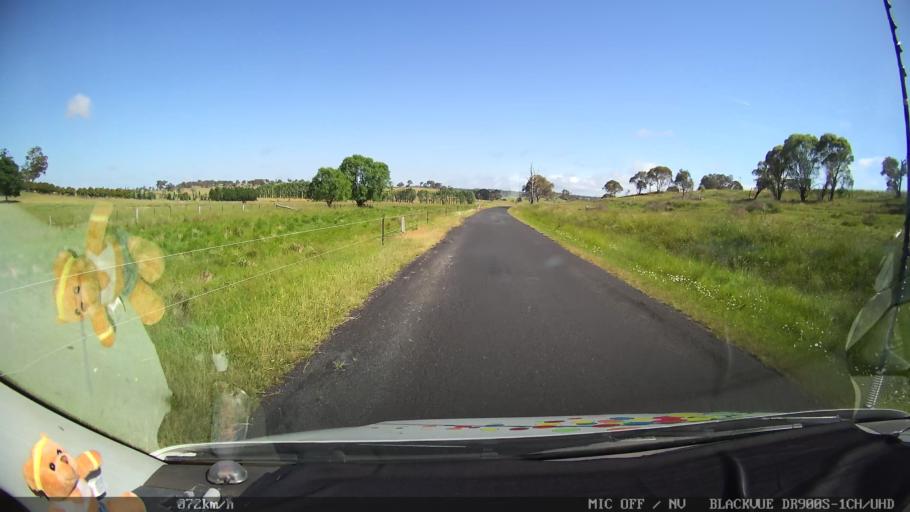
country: AU
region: New South Wales
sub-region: Guyra
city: Guyra
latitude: -30.1581
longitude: 151.6812
